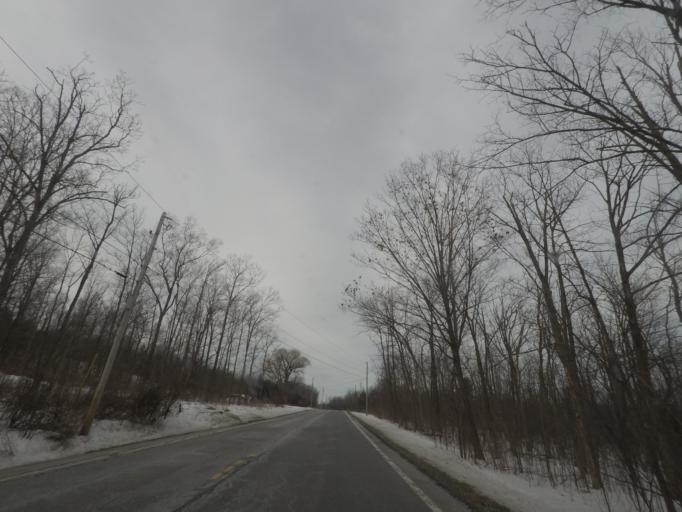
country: US
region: New York
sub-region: Albany County
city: Altamont
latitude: 42.6875
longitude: -74.0228
